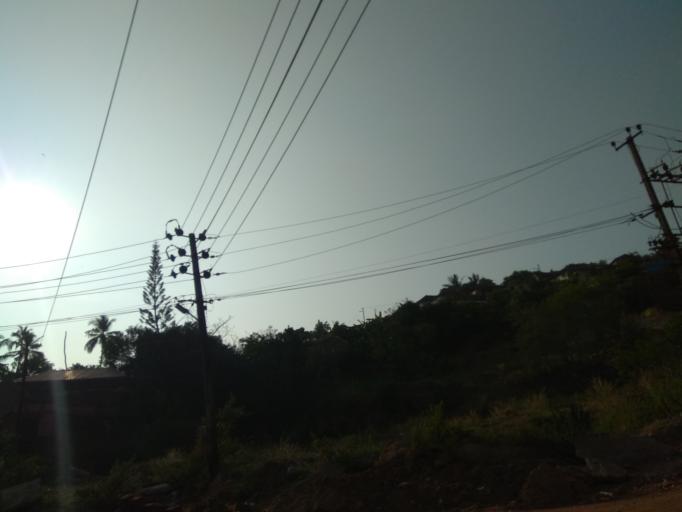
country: IN
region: Karnataka
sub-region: Dakshina Kannada
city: Mangalore
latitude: 12.9088
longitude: 74.8507
